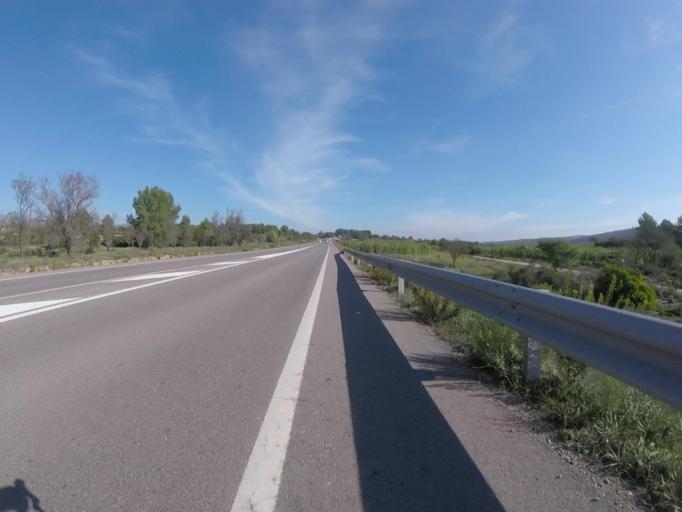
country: ES
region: Valencia
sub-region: Provincia de Castello
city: Benlloch
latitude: 40.2543
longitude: 0.0755
